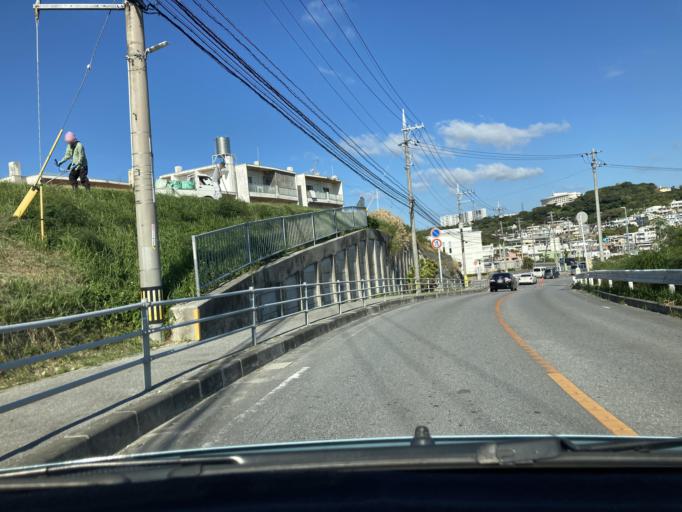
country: JP
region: Okinawa
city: Chatan
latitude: 26.2979
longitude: 127.7982
